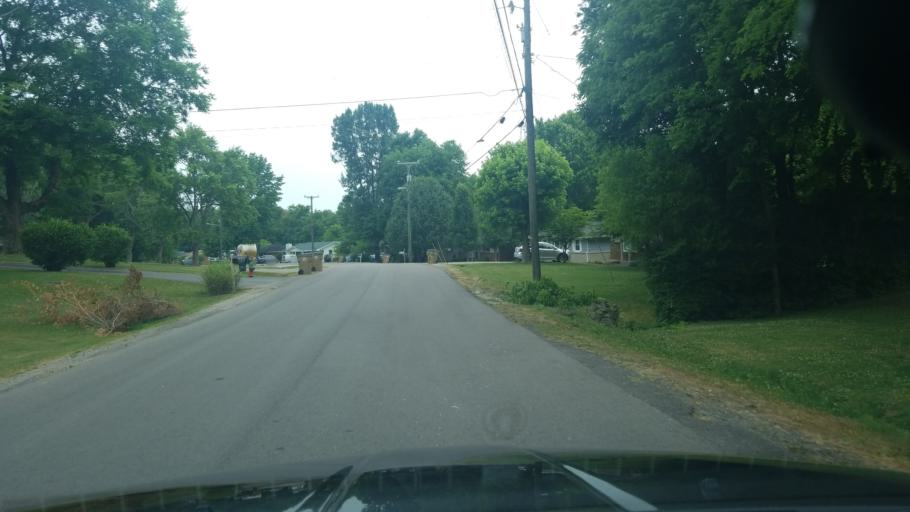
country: US
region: Tennessee
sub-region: Davidson County
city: Goodlettsville
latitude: 36.2632
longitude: -86.7455
